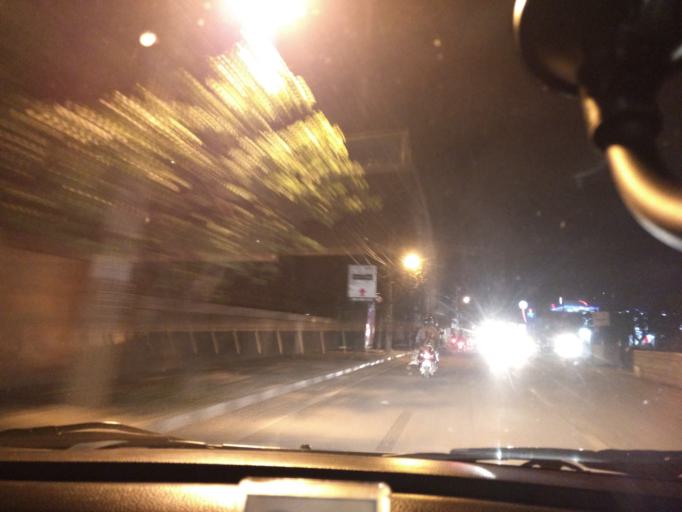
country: IN
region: Karnataka
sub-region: Bangalore Urban
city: Bangalore
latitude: 12.9153
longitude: 77.6673
